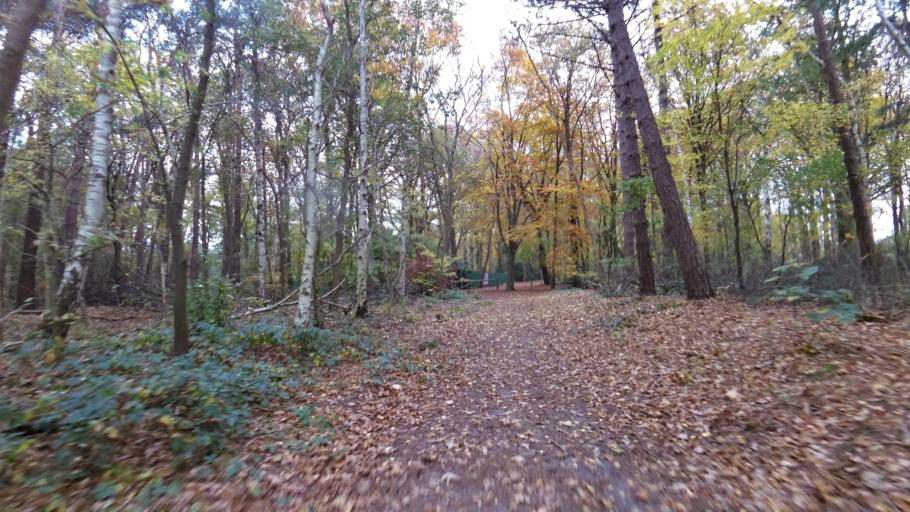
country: NL
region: North Holland
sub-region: Gemeente Hilversum
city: Hilversum
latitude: 52.2065
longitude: 5.1971
